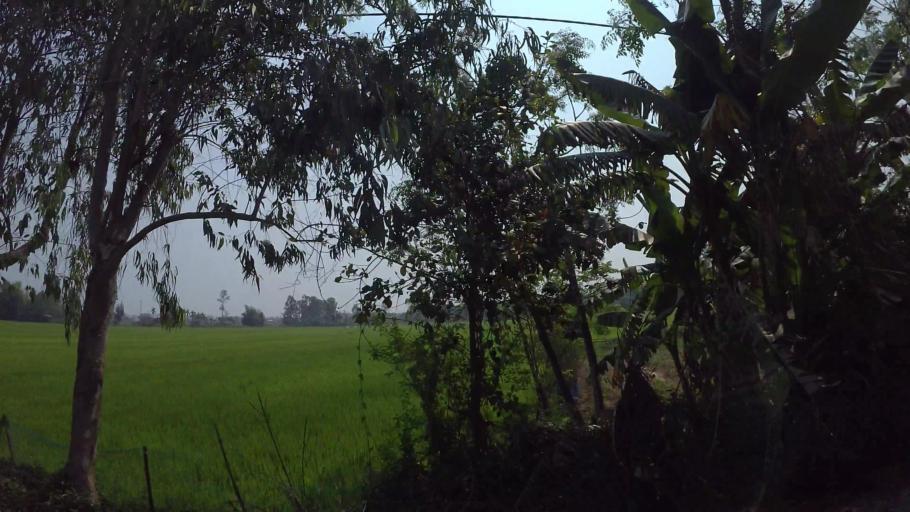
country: VN
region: Da Nang
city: Cam Le
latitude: 15.9755
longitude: 108.2268
